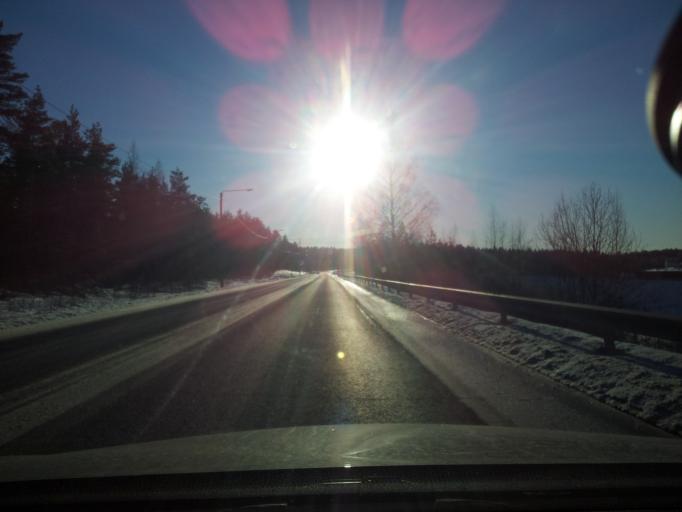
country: FI
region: Uusimaa
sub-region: Helsinki
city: Vihti
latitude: 60.3547
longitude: 24.3352
